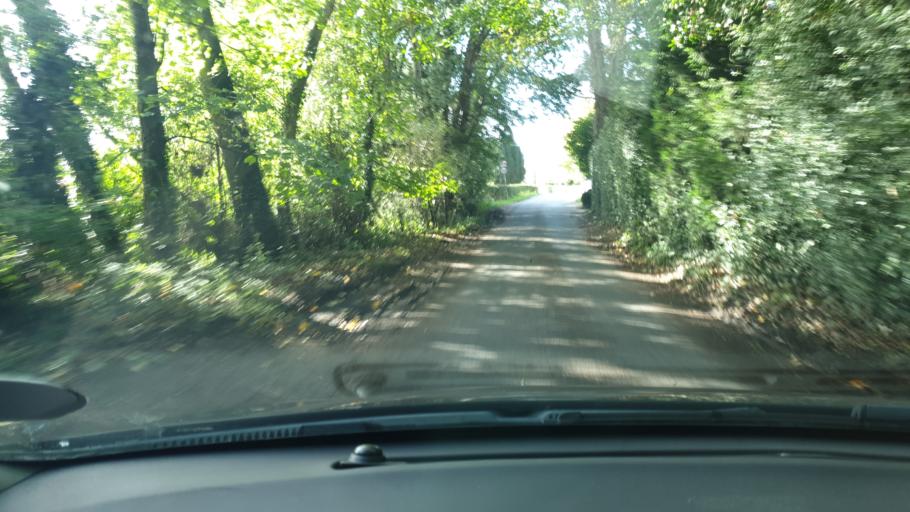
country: GB
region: England
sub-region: Essex
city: Alresford
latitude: 51.8967
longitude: 1.0280
